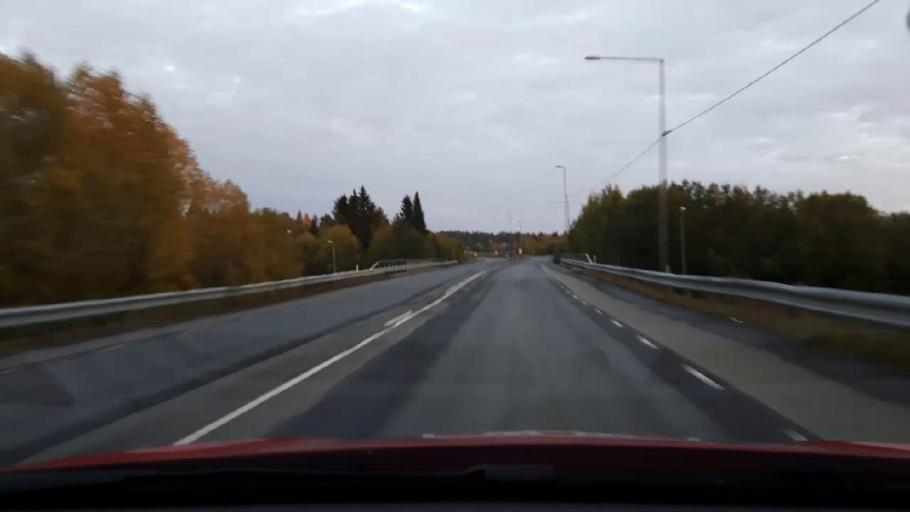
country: SE
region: Jaemtland
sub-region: OEstersunds Kommun
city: Ostersund
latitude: 63.2017
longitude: 14.6421
